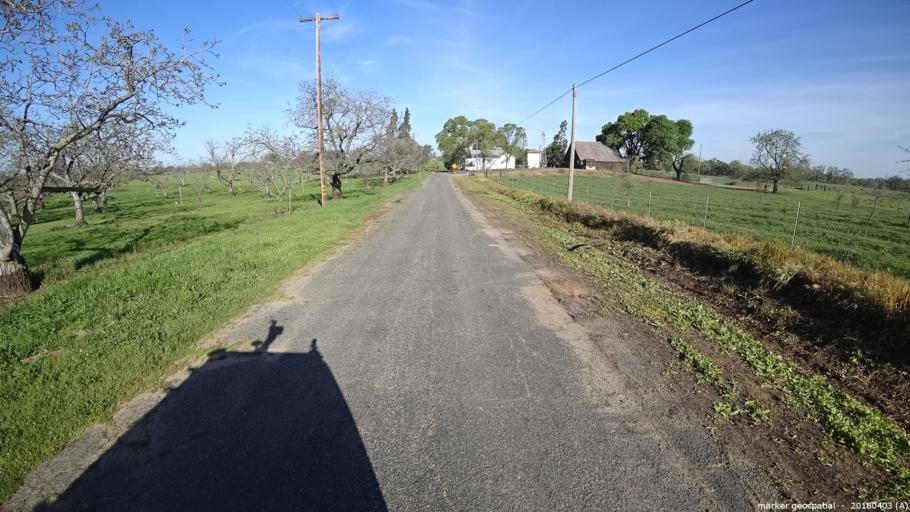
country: US
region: California
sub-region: Sacramento County
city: Wilton
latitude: 38.4419
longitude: -121.2126
